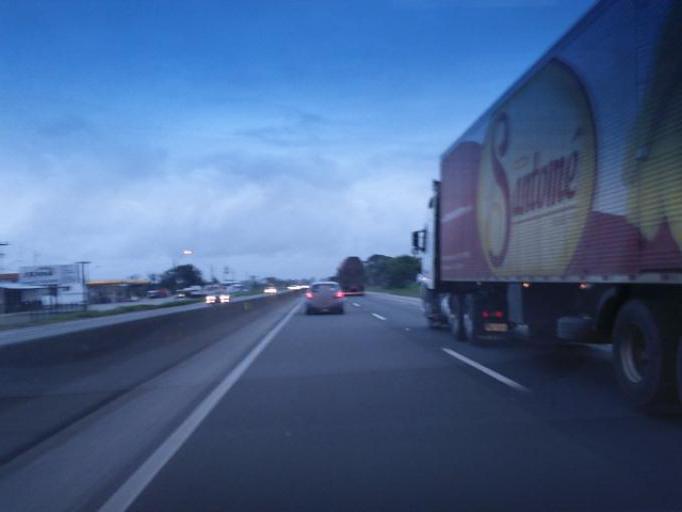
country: BR
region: Santa Catarina
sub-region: Barra Velha
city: Barra Velha
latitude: -26.5268
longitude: -48.7155
